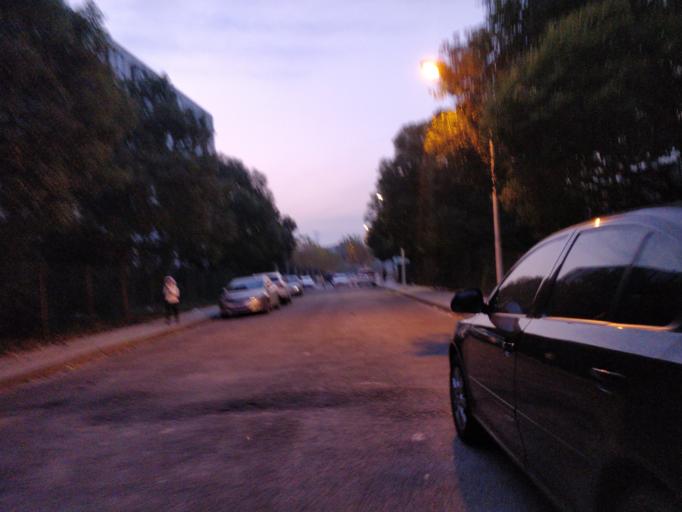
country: CN
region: Shanghai Shi
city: Huangdu
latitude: 31.2906
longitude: 121.2137
